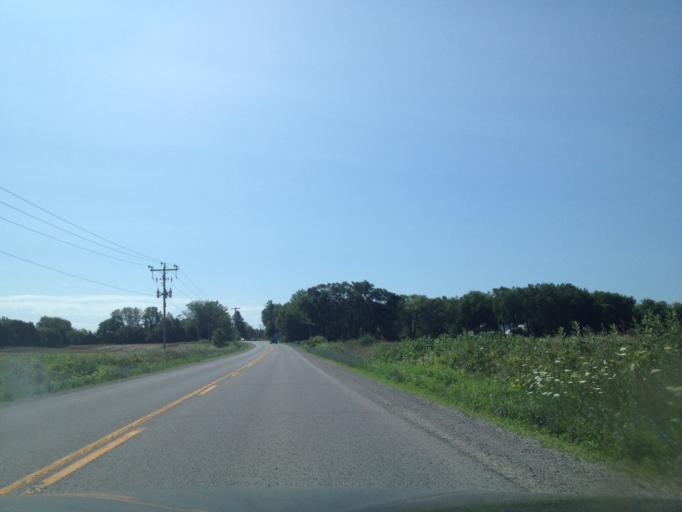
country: CA
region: Ontario
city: Norfolk County
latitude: 42.7776
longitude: -80.3990
